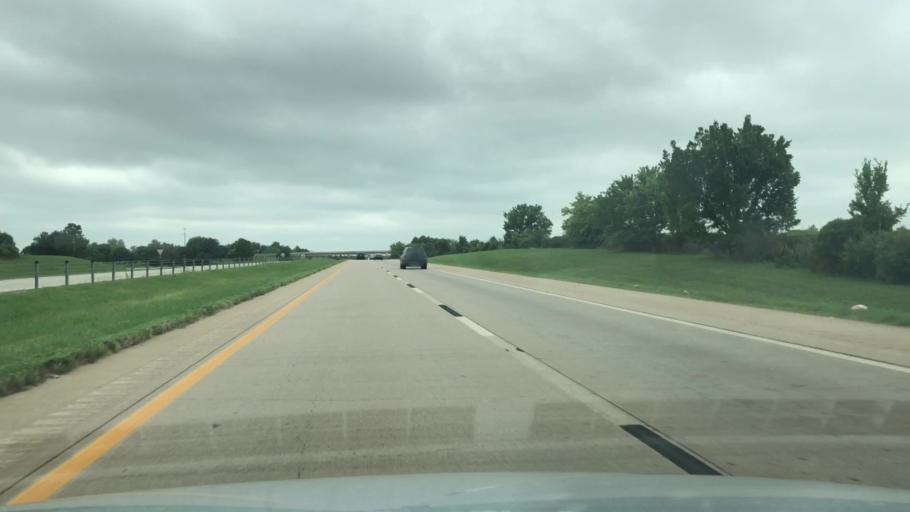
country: US
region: Oklahoma
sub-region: Tulsa County
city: Turley
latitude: 36.2690
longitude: -95.9239
